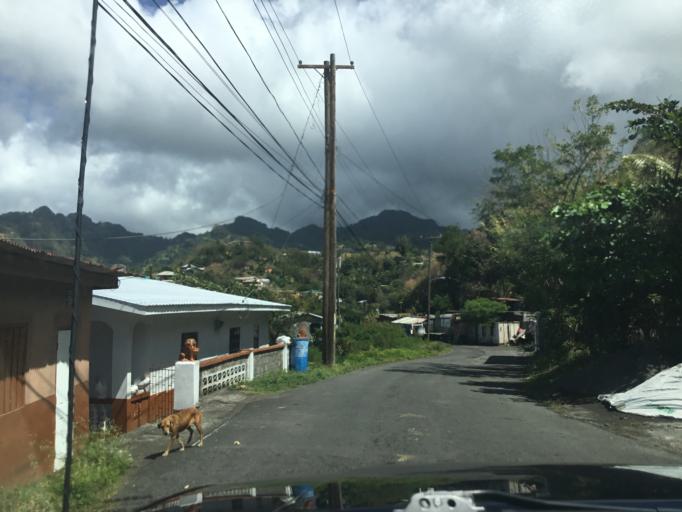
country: VC
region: Saint George
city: Kingstown Park
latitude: 13.1617
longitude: -61.2384
